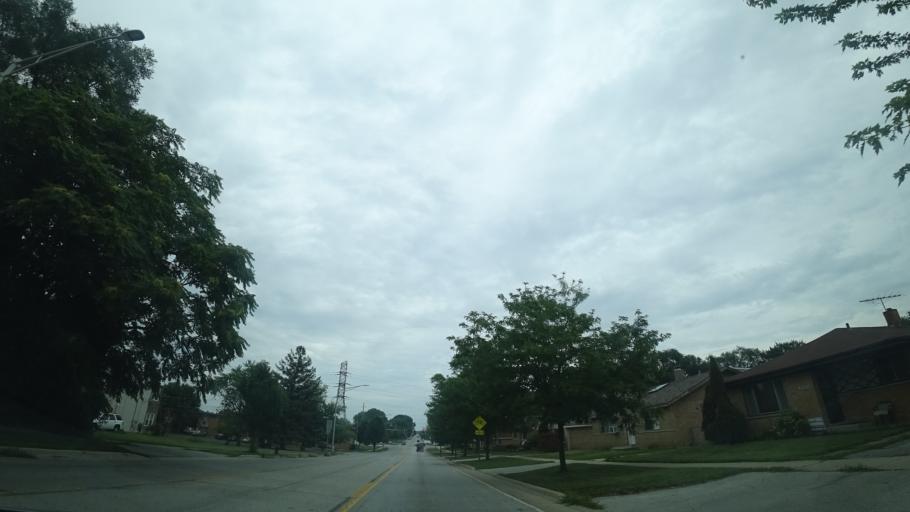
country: US
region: Illinois
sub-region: Cook County
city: Alsip
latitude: 41.6692
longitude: -87.7314
